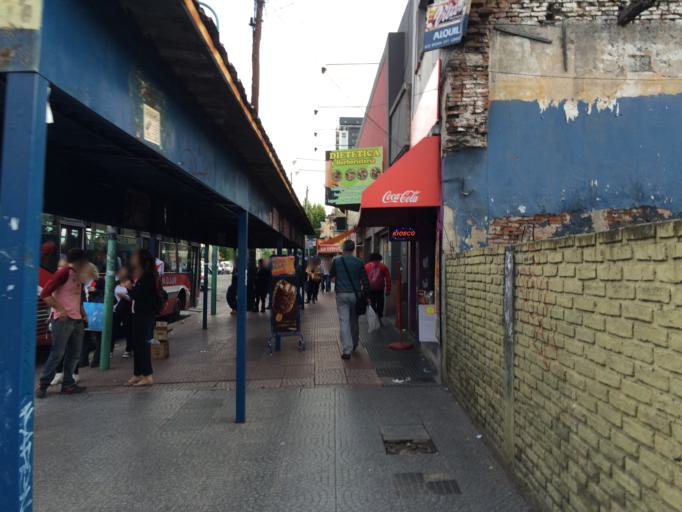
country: AR
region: Buenos Aires
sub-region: Partido de Lomas de Zamora
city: Lomas de Zamora
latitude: -34.7608
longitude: -58.3964
